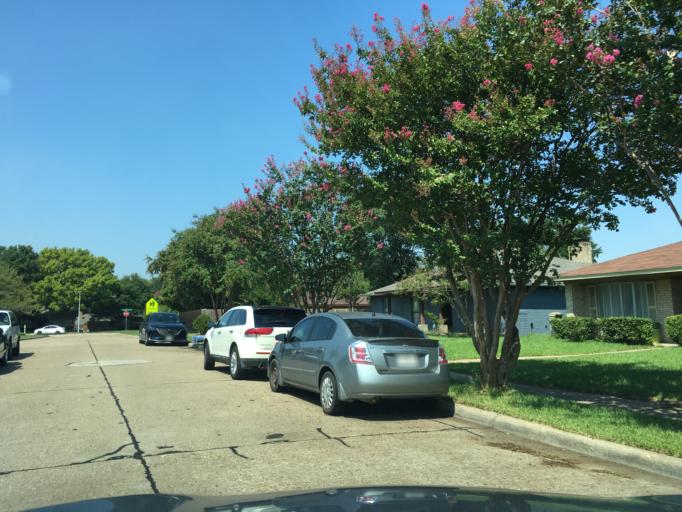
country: US
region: Texas
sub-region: Dallas County
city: Garland
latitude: 32.9372
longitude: -96.6561
